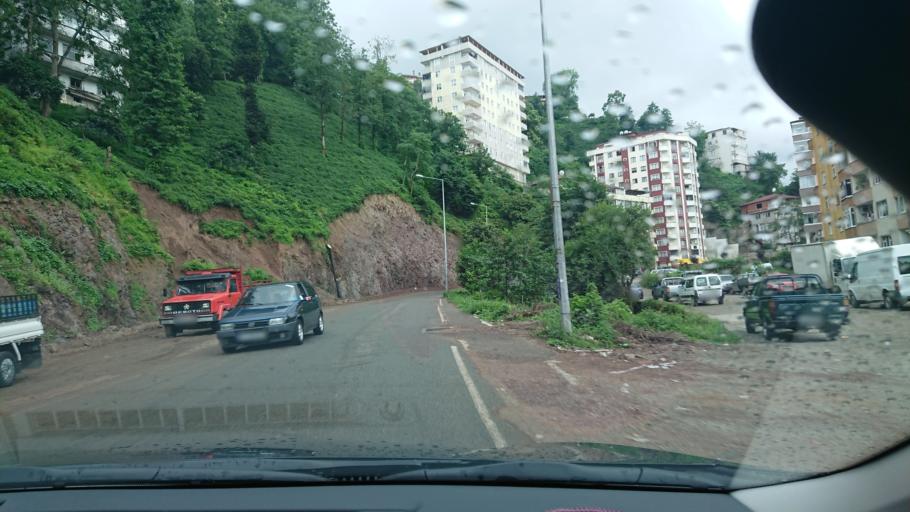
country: TR
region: Rize
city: Rize
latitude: 41.0256
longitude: 40.5130
